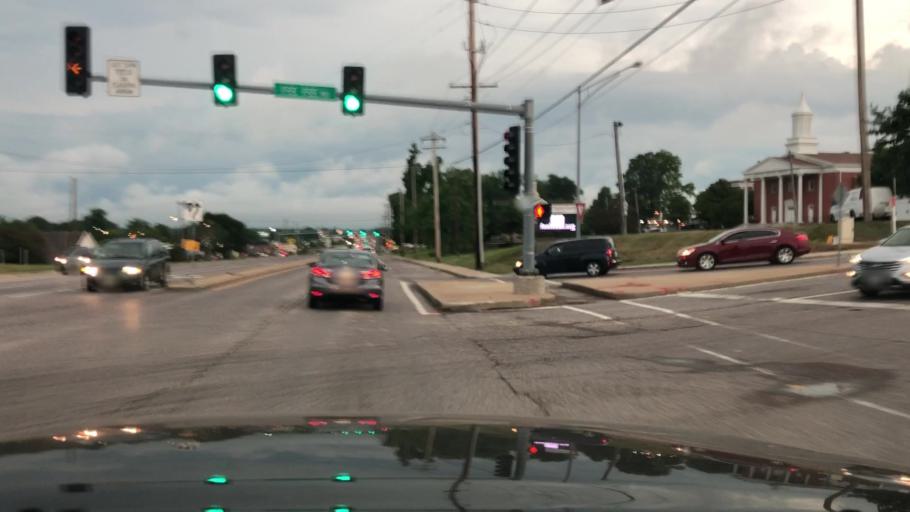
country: US
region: Missouri
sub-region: Saint Louis County
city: Saint Ann
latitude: 38.7404
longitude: -90.4039
